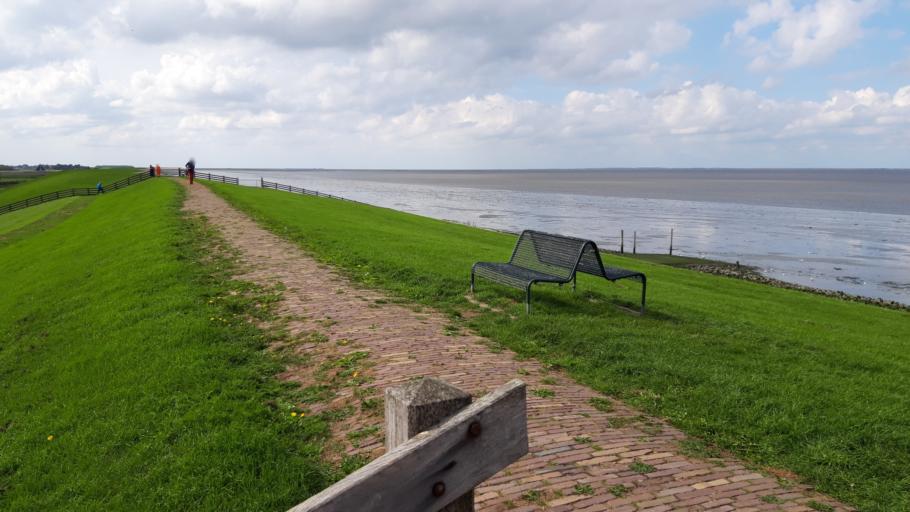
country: NL
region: Friesland
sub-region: Gemeente Dongeradeel
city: Ternaard
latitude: 53.4024
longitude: 6.0152
